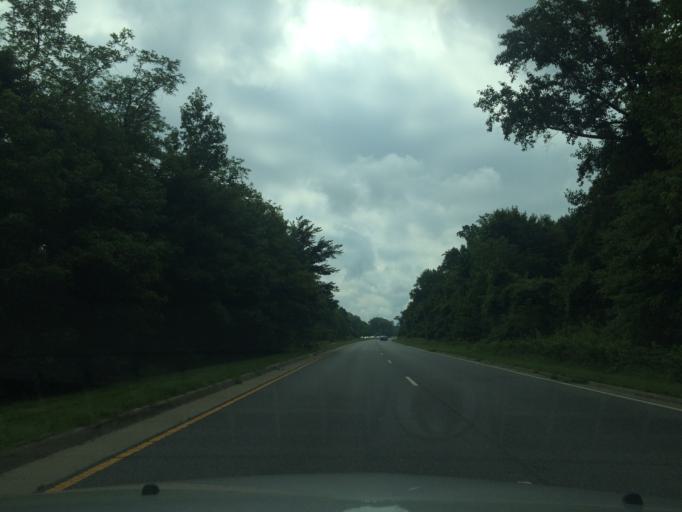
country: US
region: Maryland
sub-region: Prince George's County
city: Morningside
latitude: 38.8345
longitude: -76.8871
